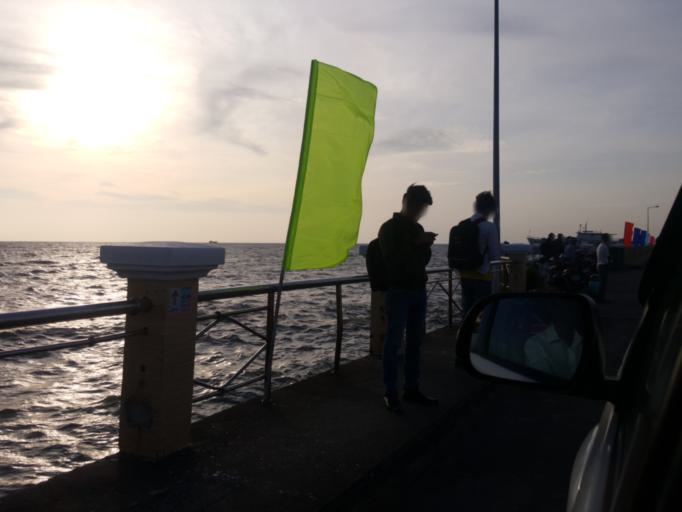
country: VN
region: Kien Giang
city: Duong GJong
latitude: 10.1474
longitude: 104.0382
